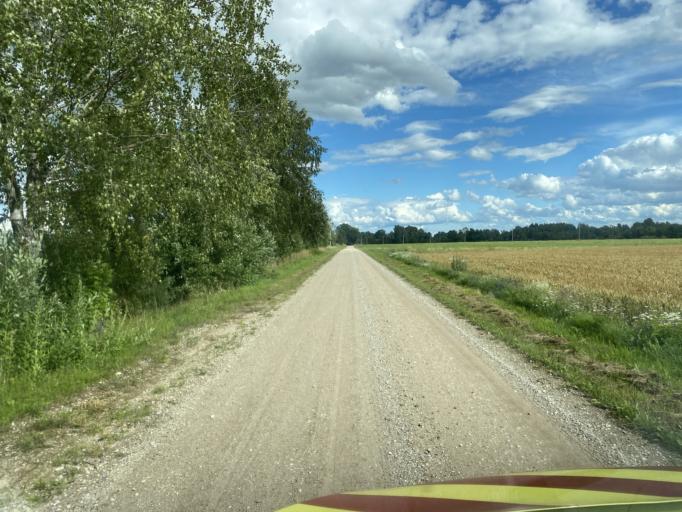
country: EE
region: Viljandimaa
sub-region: Viiratsi vald
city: Viiratsi
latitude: 58.3988
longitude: 25.8105
